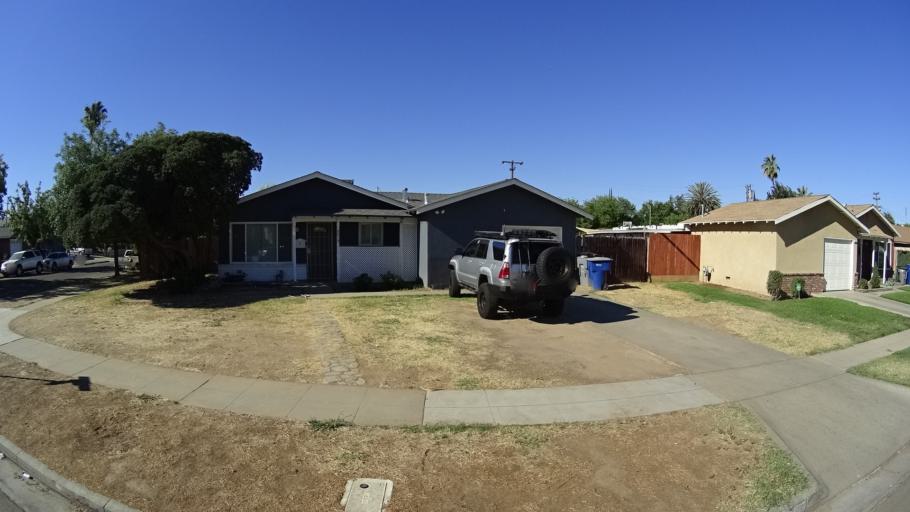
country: US
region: California
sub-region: Fresno County
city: Fresno
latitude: 36.7960
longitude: -119.8372
